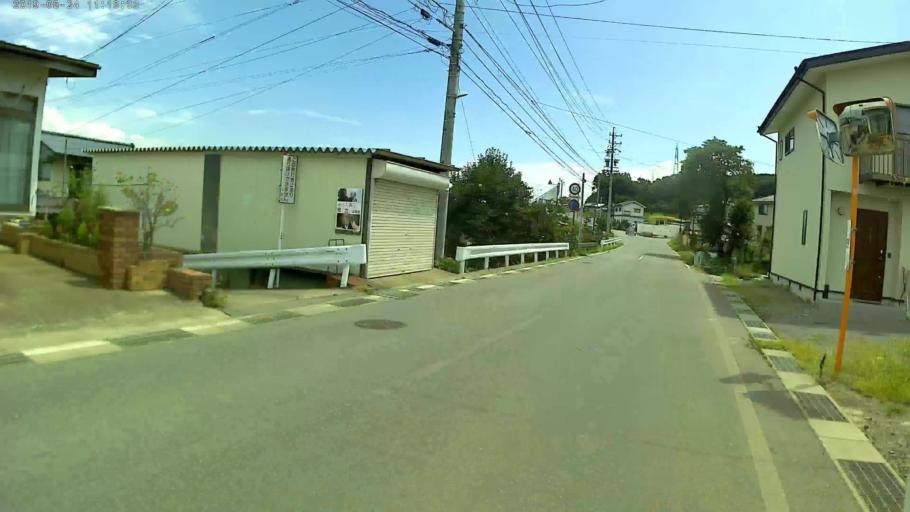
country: JP
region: Nagano
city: Kamimaruko
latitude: 36.2718
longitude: 138.3222
